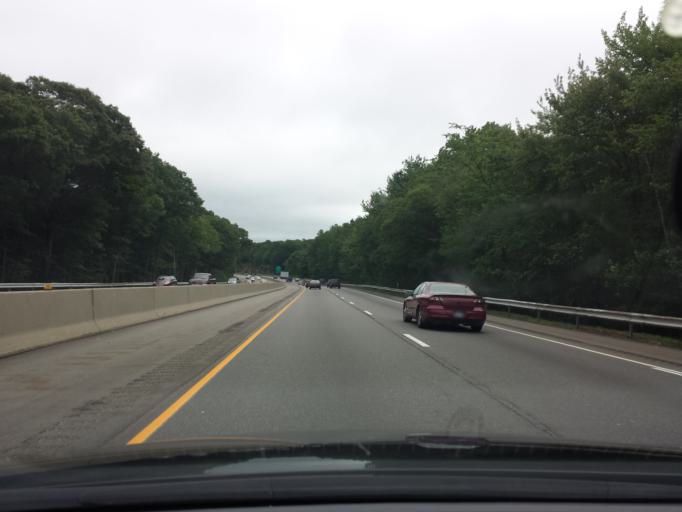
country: US
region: Connecticut
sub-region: Middlesex County
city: Clinton
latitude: 41.2892
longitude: -72.5076
